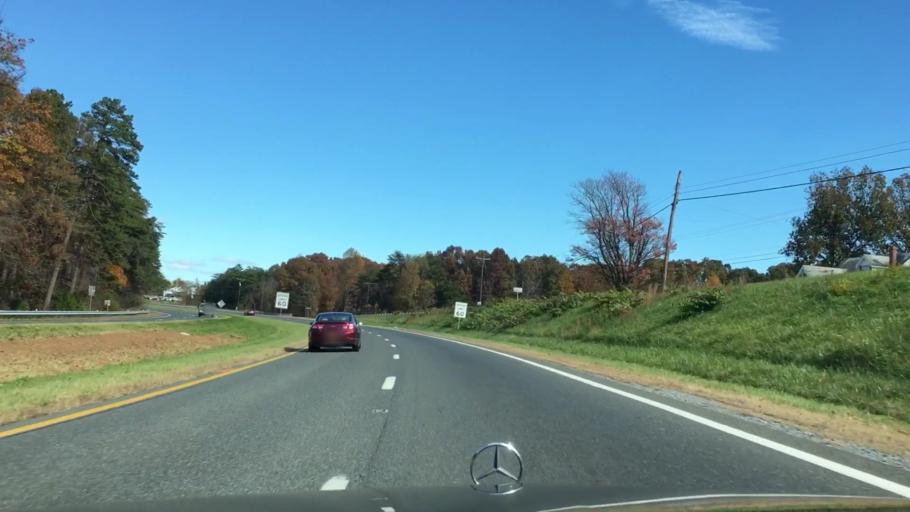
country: US
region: Virginia
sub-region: Campbell County
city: Altavista
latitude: 37.1478
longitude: -79.2300
